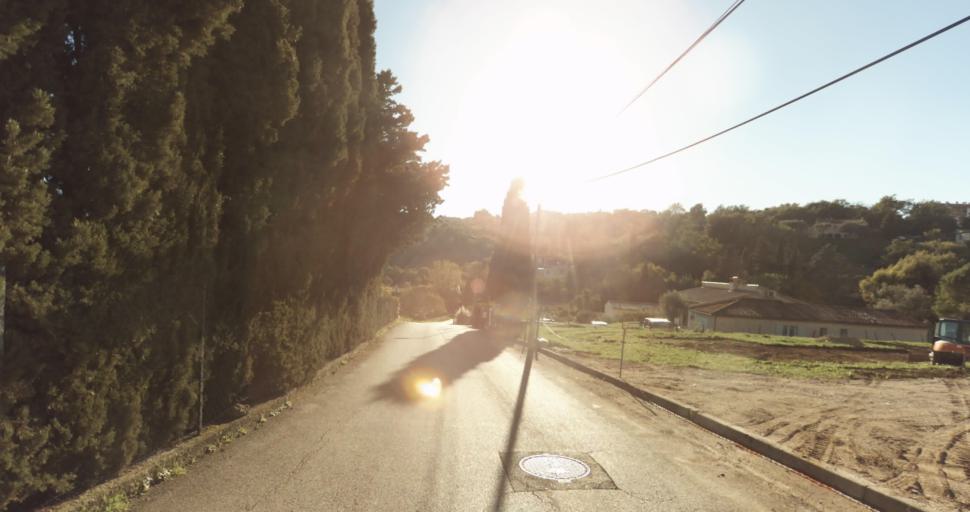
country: FR
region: Provence-Alpes-Cote d'Azur
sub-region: Departement des Alpes-Maritimes
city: Vence
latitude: 43.7264
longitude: 7.1267
